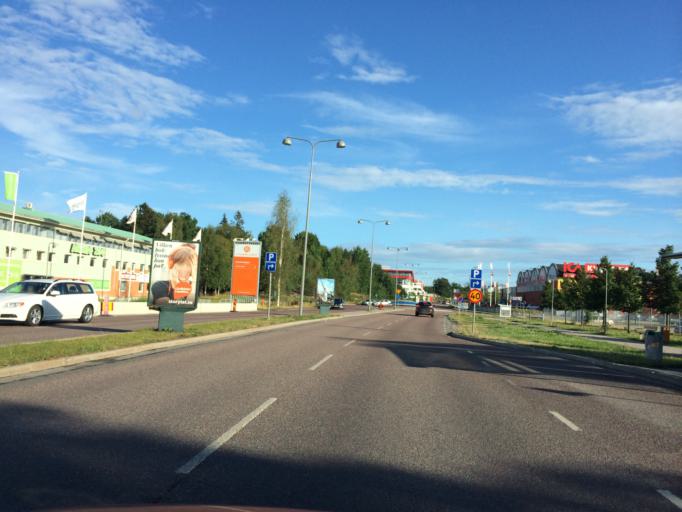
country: SE
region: Stockholm
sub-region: Huddinge Kommun
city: Segeltorp
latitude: 59.2727
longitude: 17.9203
